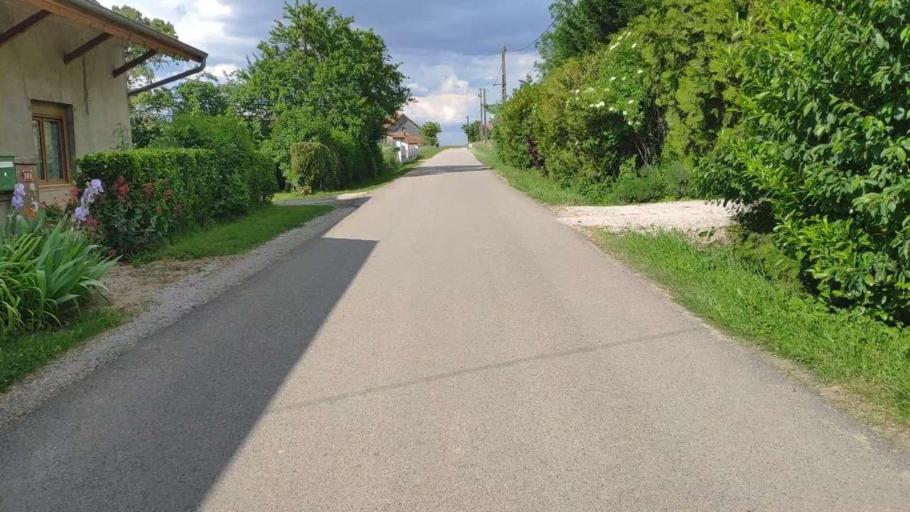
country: FR
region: Franche-Comte
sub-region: Departement du Jura
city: Bletterans
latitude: 46.8121
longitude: 5.3777
